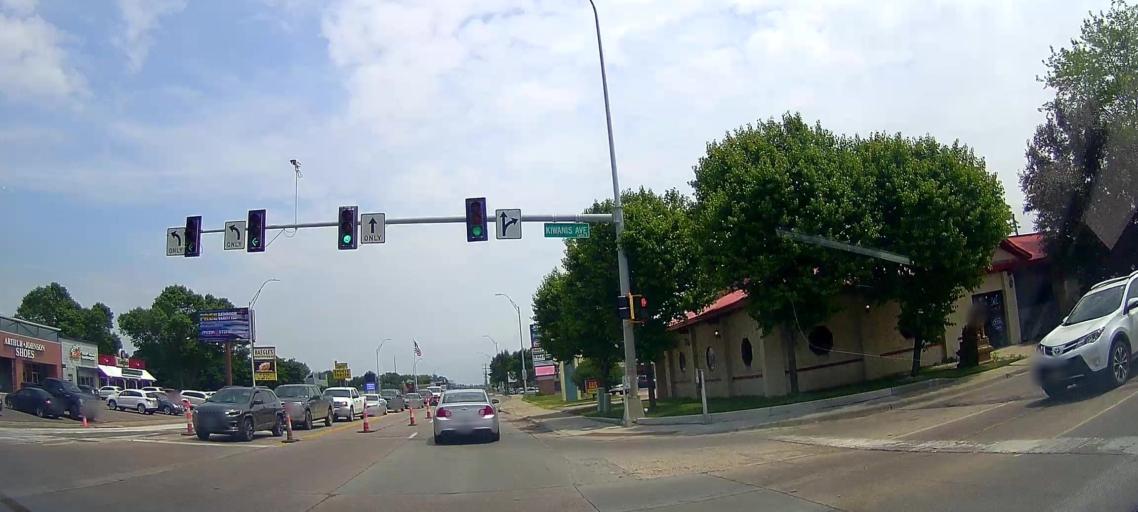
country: US
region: South Dakota
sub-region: Minnehaha County
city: Sioux Falls
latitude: 43.5148
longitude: -96.7609
